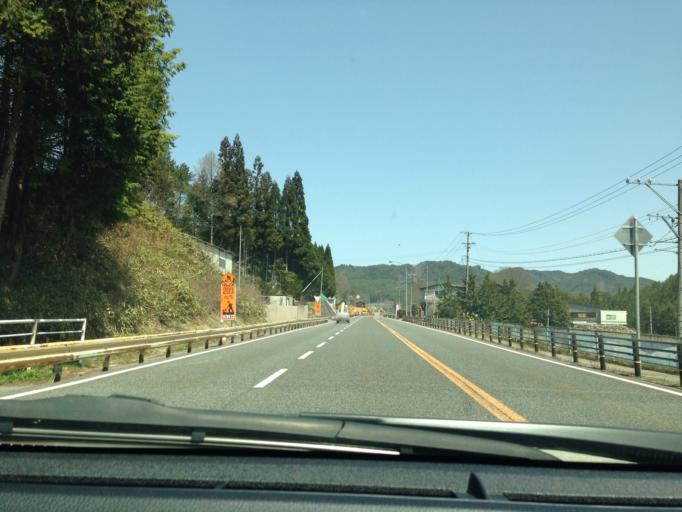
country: JP
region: Gifu
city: Takayama
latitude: 36.0668
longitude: 137.2676
